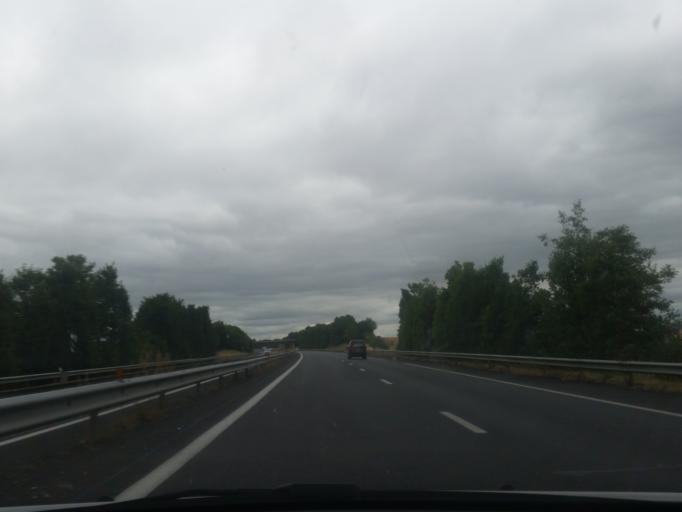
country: FR
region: Pays de la Loire
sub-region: Departement de la Sarthe
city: Noyen-sur-Sarthe
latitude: 47.8571
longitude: -0.1186
